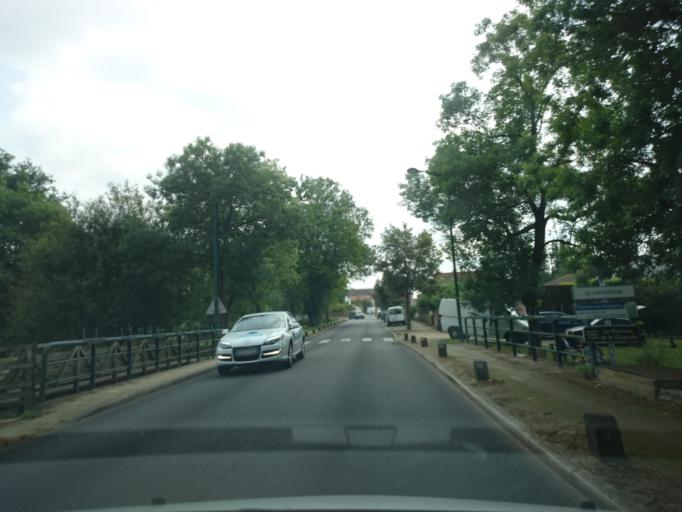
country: FR
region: Pays de la Loire
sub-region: Departement de la Loire-Atlantique
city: La Chevroliere
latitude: 47.0972
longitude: -1.6112
